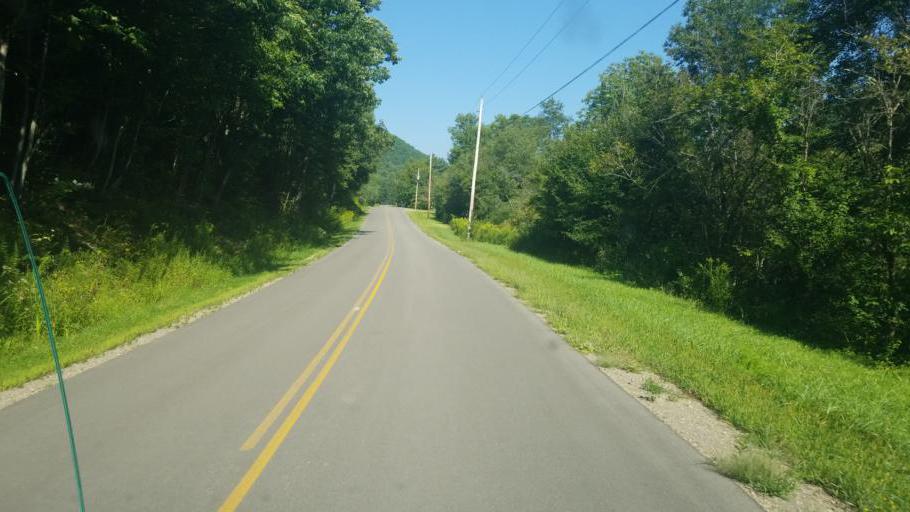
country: US
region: New York
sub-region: Allegany County
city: Wellsville
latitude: 42.0139
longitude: -78.0091
